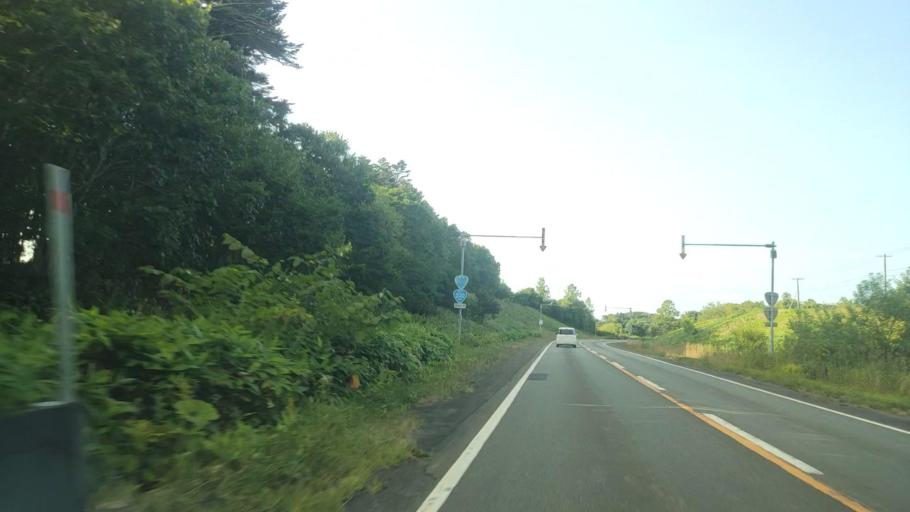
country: JP
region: Hokkaido
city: Makubetsu
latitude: 45.0661
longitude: 141.7482
